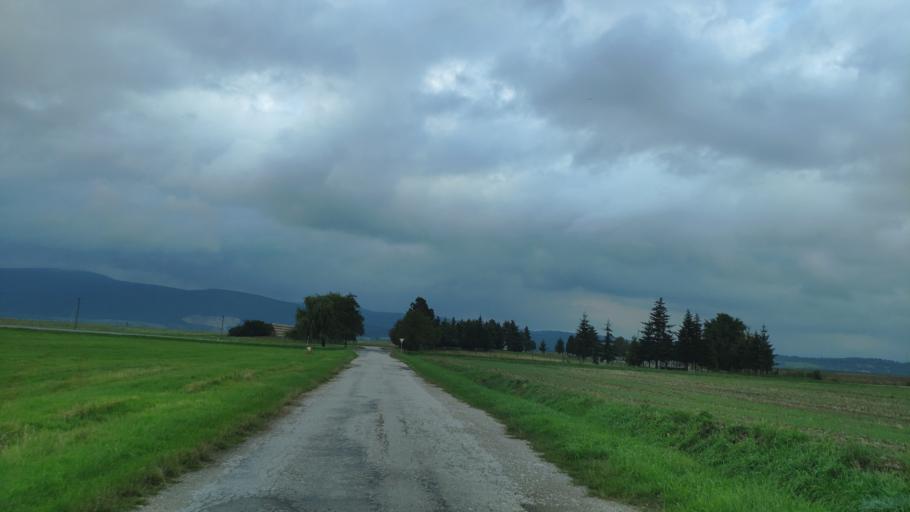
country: SK
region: Kosicky
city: Moldava nad Bodvou
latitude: 48.5792
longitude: 20.9555
